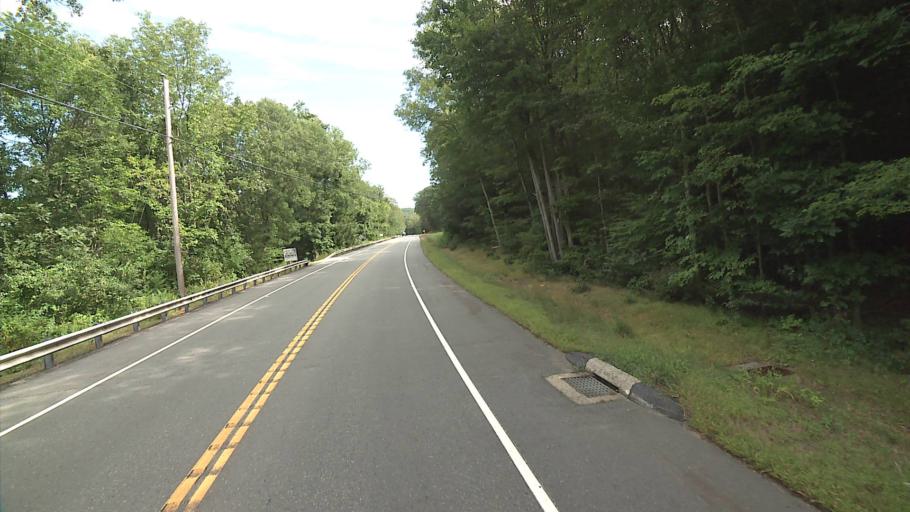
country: US
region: Connecticut
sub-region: Tolland County
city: South Coventry
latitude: 41.8279
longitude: -72.3096
